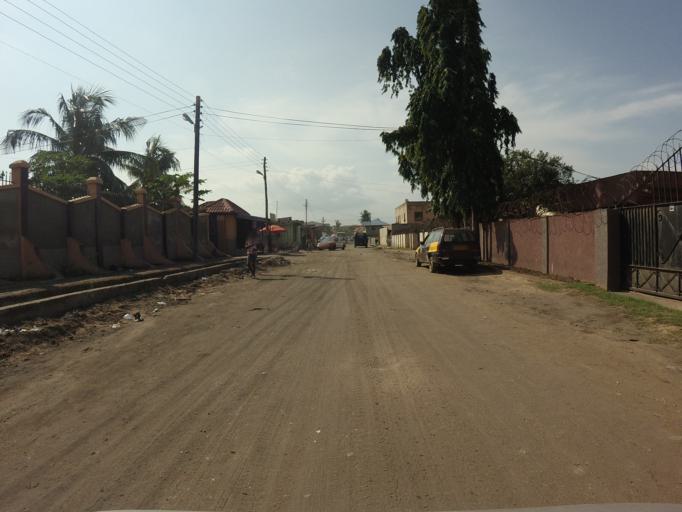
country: GH
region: Greater Accra
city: Dome
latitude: 5.6429
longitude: -0.2350
